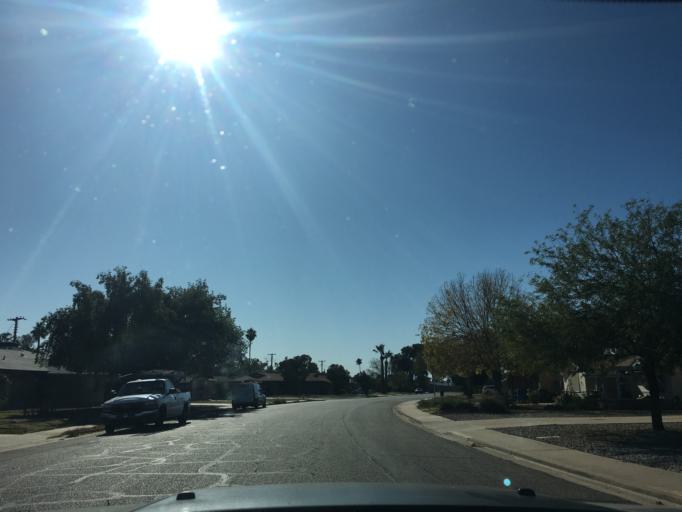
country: US
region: Arizona
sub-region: Maricopa County
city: Mesa
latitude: 33.4465
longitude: -111.8480
